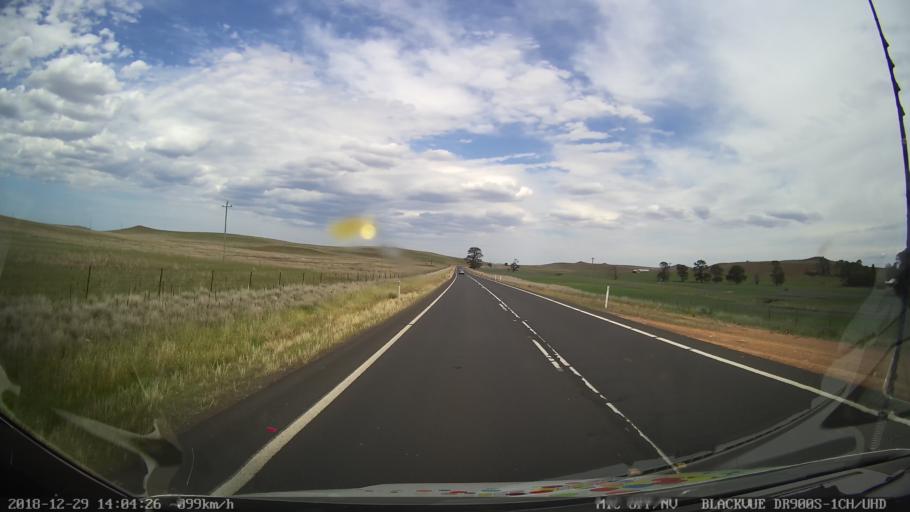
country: AU
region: New South Wales
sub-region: Cooma-Monaro
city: Cooma
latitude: -36.3161
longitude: 149.1866
